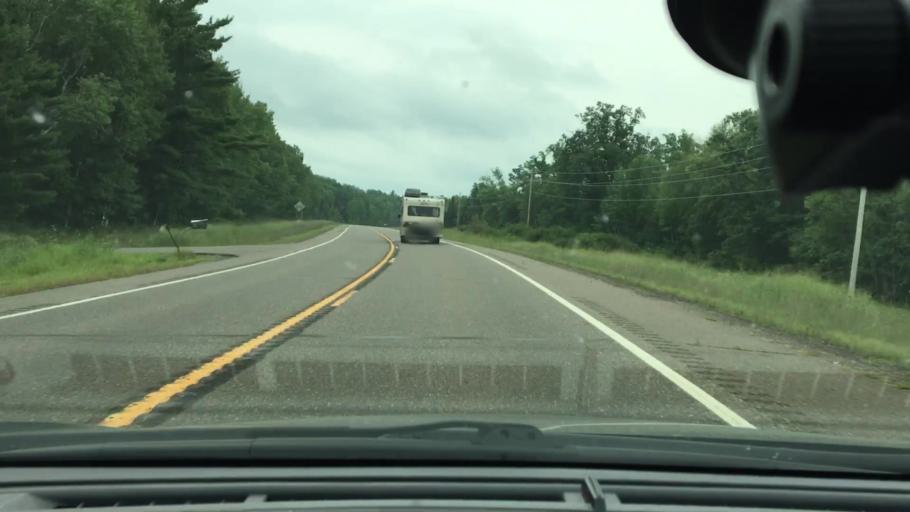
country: US
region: Minnesota
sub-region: Crow Wing County
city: Crosby
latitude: 46.5075
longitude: -93.9597
